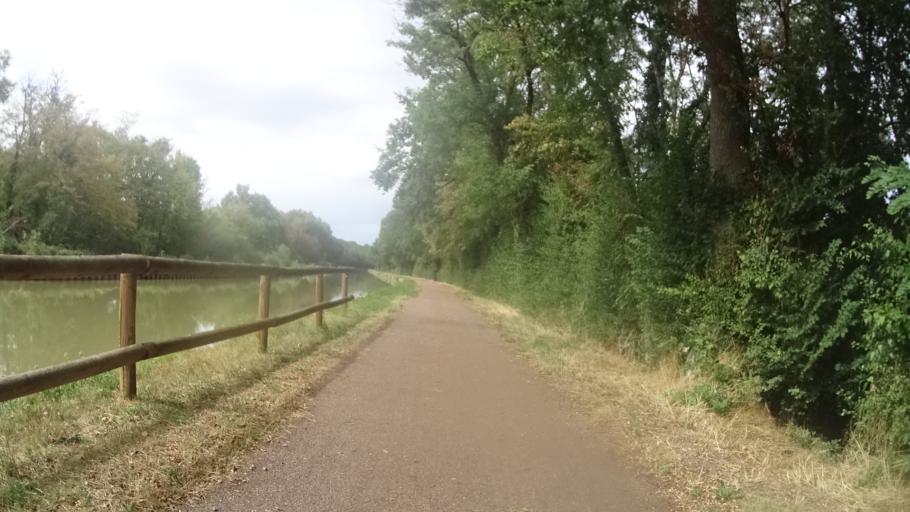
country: FR
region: Bourgogne
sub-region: Departement de la Nievre
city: Sermoise-sur-Loire
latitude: 46.9472
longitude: 3.2027
